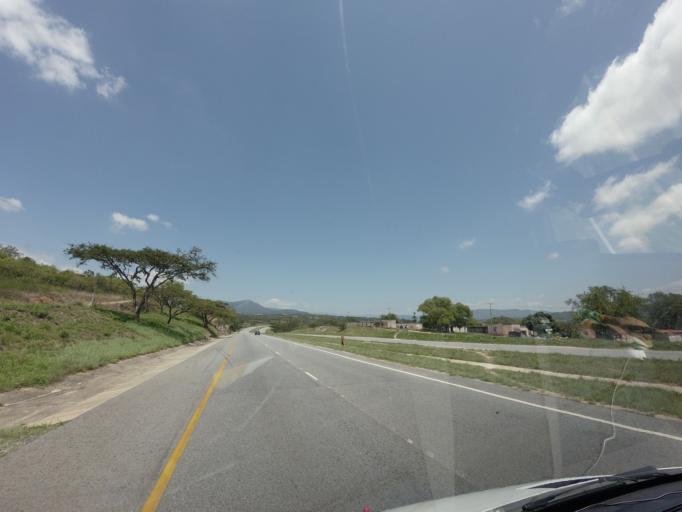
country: ZA
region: Mpumalanga
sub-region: Ehlanzeni District
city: Nelspruit
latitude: -25.4456
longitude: 30.8709
